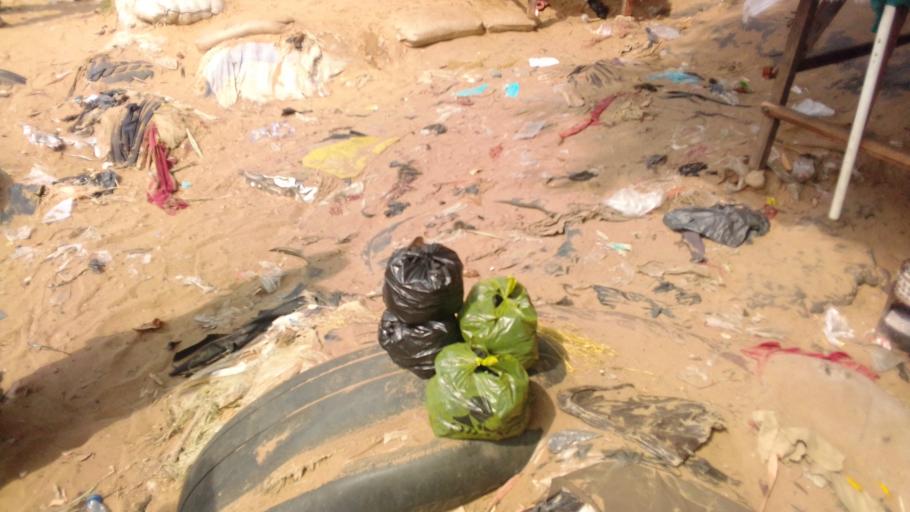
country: CD
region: Kinshasa
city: Masina
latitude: -4.3991
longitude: 15.3449
